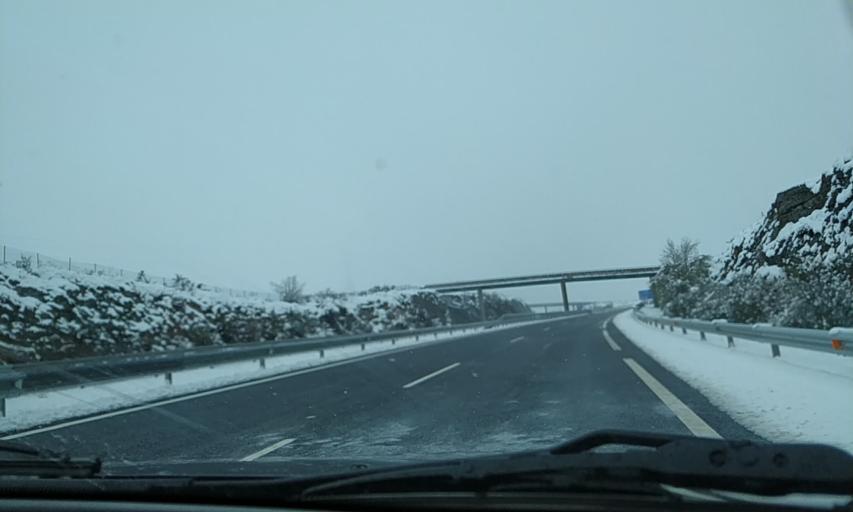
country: ES
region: Castille and Leon
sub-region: Provincia de Zamora
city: Pias
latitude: 42.0416
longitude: -7.0433
